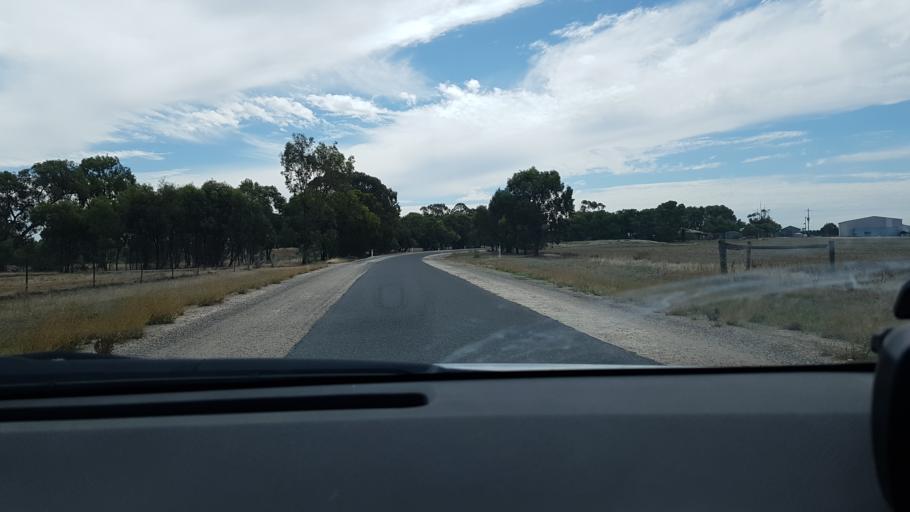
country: AU
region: Victoria
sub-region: Horsham
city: Horsham
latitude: -36.7224
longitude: 141.7790
